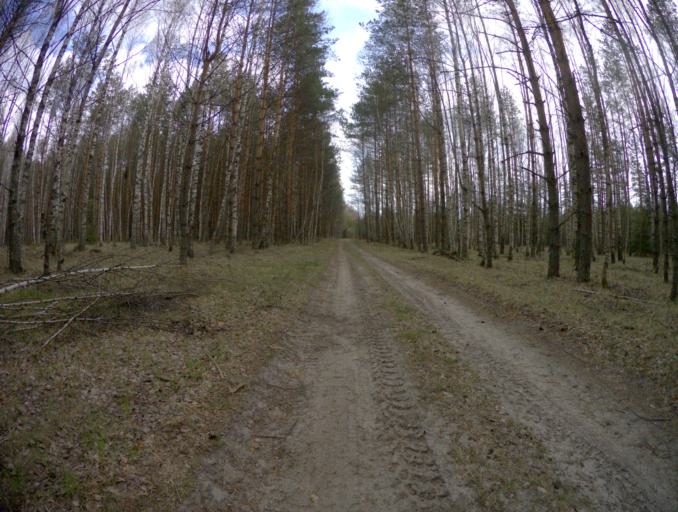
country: RU
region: Vladimir
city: Orgtrud
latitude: 56.0728
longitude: 40.7221
